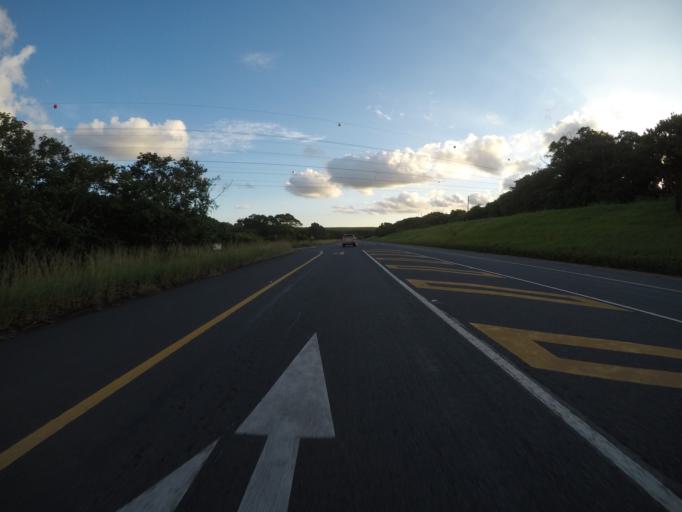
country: ZA
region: KwaZulu-Natal
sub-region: uThungulu District Municipality
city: Richards Bay
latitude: -28.6876
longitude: 32.0389
